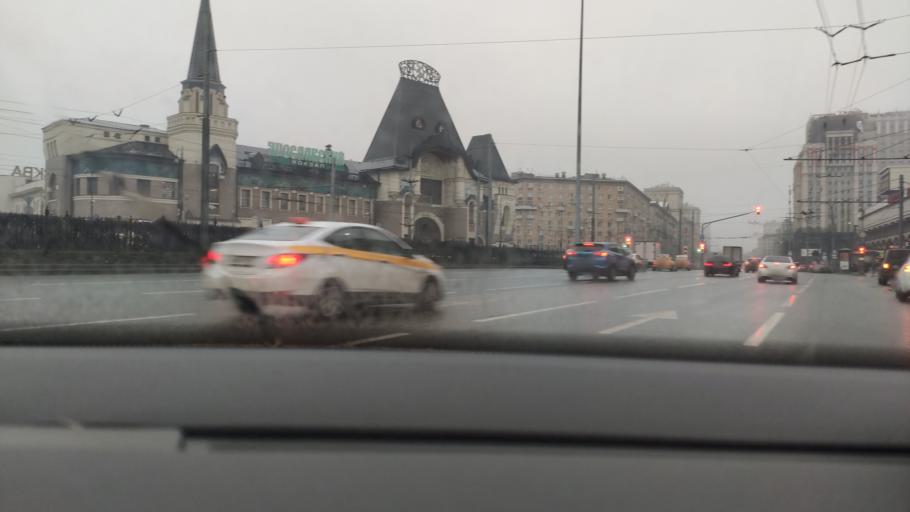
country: RU
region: Moscow
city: Sokol'niki
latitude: 55.7738
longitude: 37.6596
